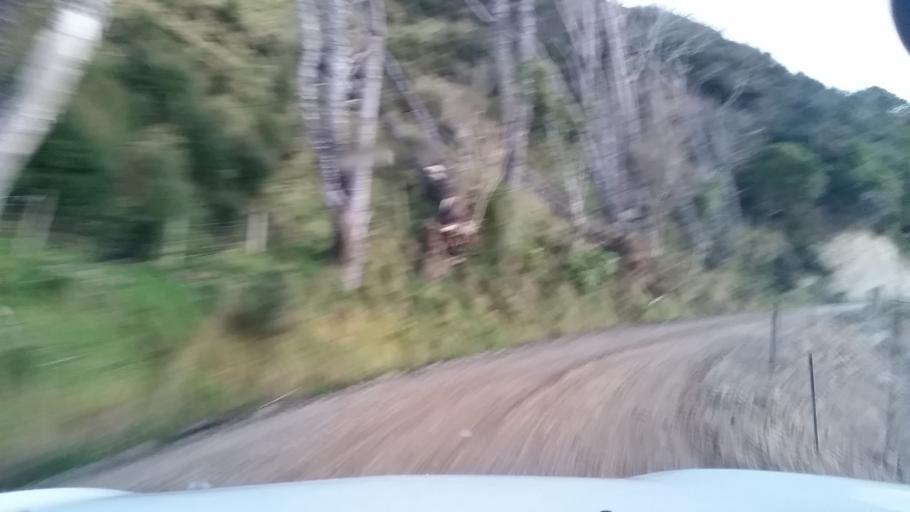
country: NZ
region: Manawatu-Wanganui
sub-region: Wanganui District
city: Wanganui
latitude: -39.7647
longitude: 174.8763
